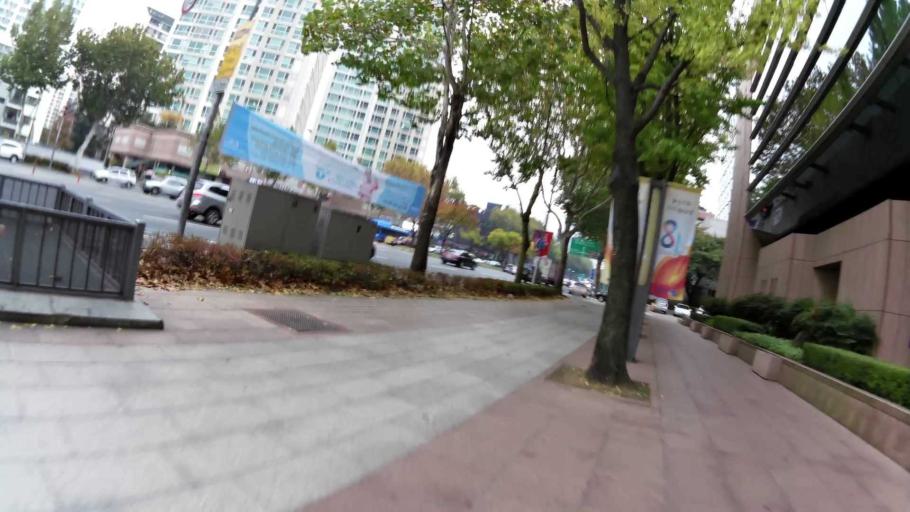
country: KR
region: Daegu
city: Daegu
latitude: 35.8595
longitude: 128.6150
